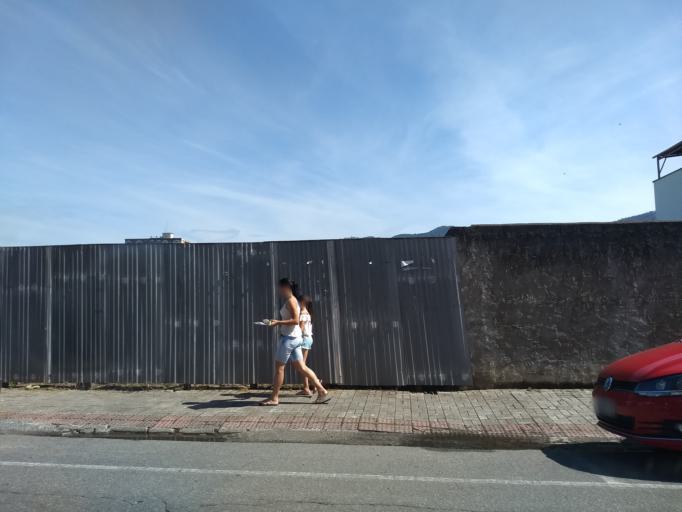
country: BR
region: Santa Catarina
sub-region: Jaragua Do Sul
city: Jaragua do Sul
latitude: -26.4914
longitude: -49.0816
